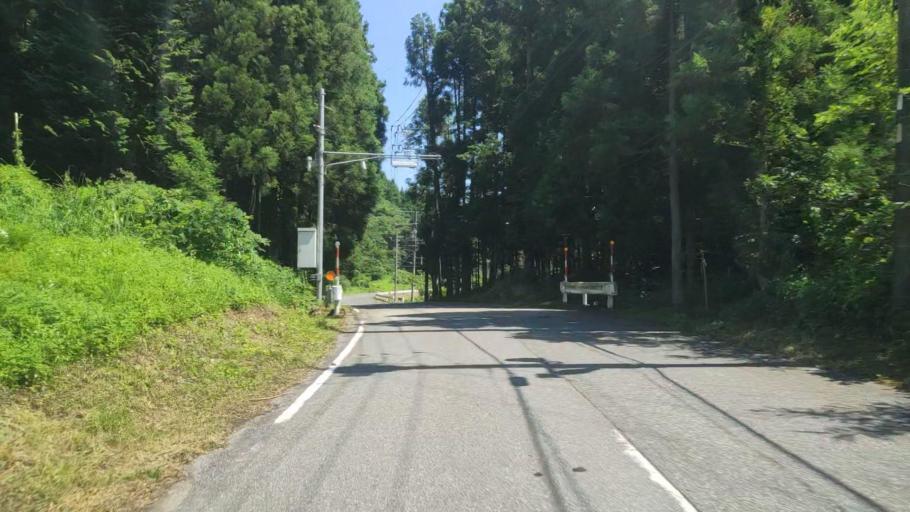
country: JP
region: Gifu
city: Godo
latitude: 35.6755
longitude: 136.5743
